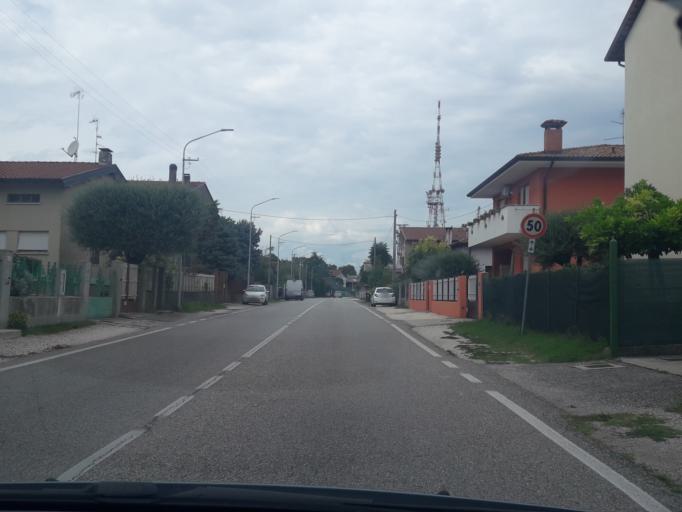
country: IT
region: Friuli Venezia Giulia
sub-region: Provincia di Udine
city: Udine
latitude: 46.0343
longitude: 13.2585
